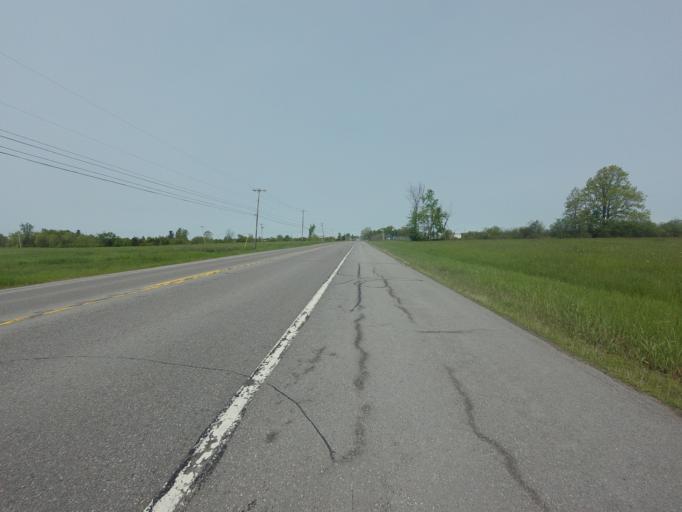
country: US
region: New York
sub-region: Jefferson County
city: Dexter
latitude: 44.0491
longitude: -76.0960
